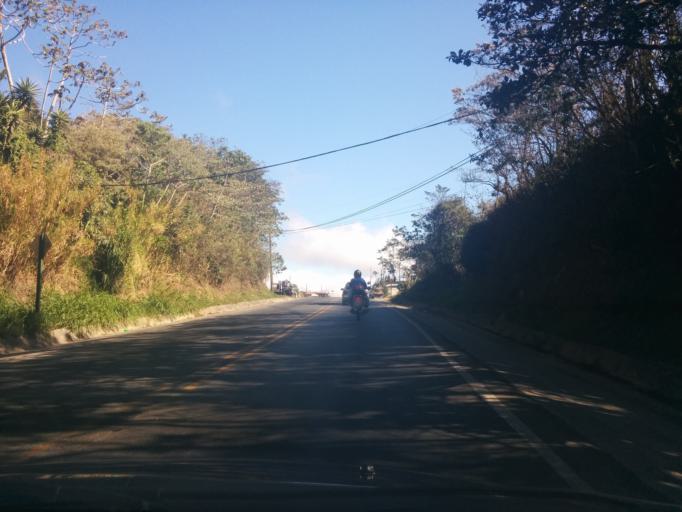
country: CR
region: Alajuela
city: San Rafael
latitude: 10.0465
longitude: -84.5067
